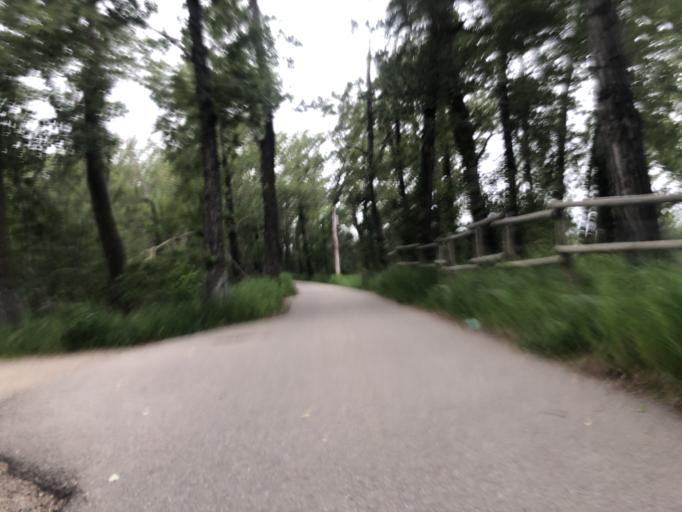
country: CA
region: Alberta
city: Calgary
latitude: 51.0430
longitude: -114.0153
